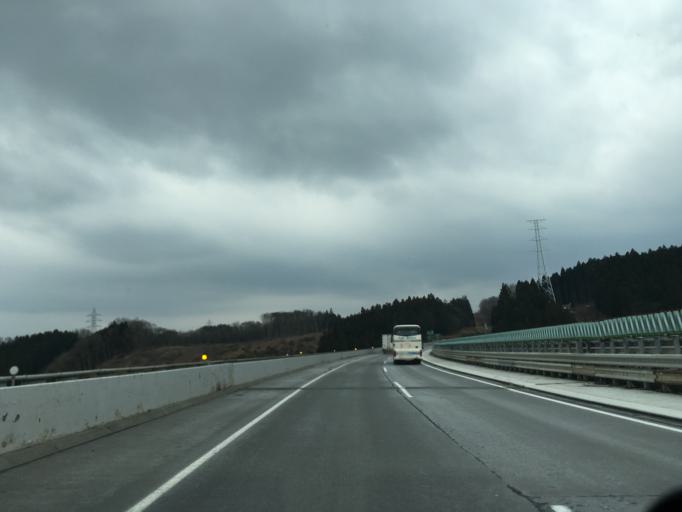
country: JP
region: Tochigi
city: Kuroiso
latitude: 37.1035
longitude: 140.1433
